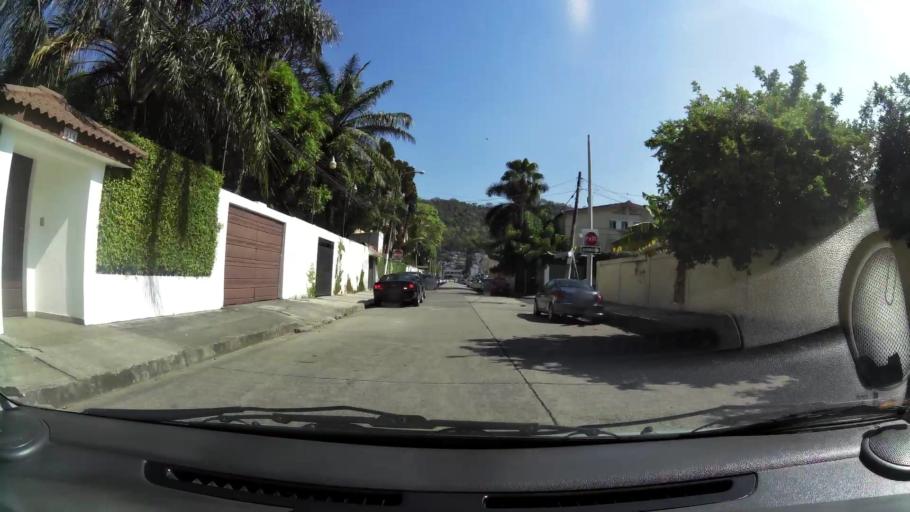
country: EC
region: Guayas
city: Guayaquil
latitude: -2.1668
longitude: -79.9173
